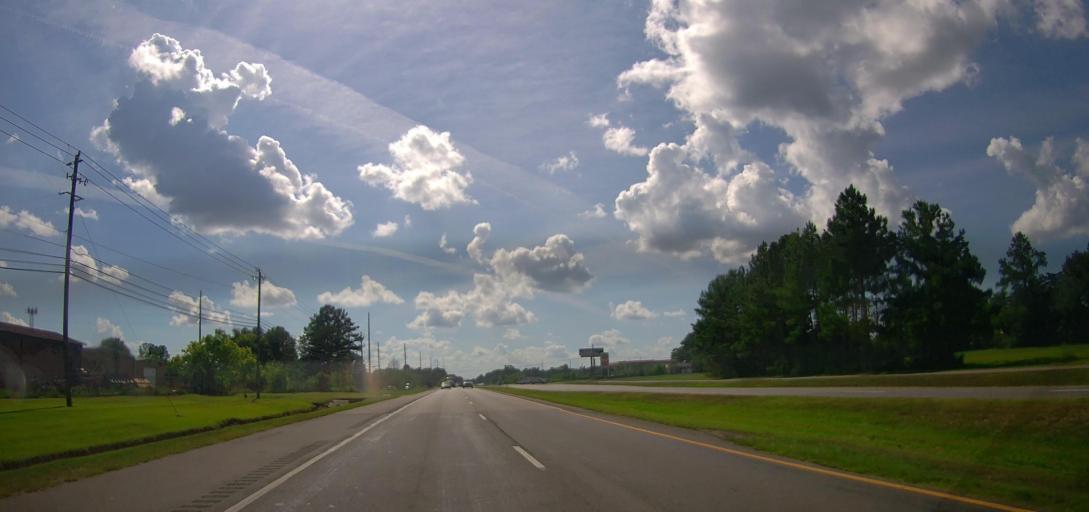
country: US
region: Alabama
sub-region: Tuscaloosa County
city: Northport
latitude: 33.2326
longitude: -87.6264
